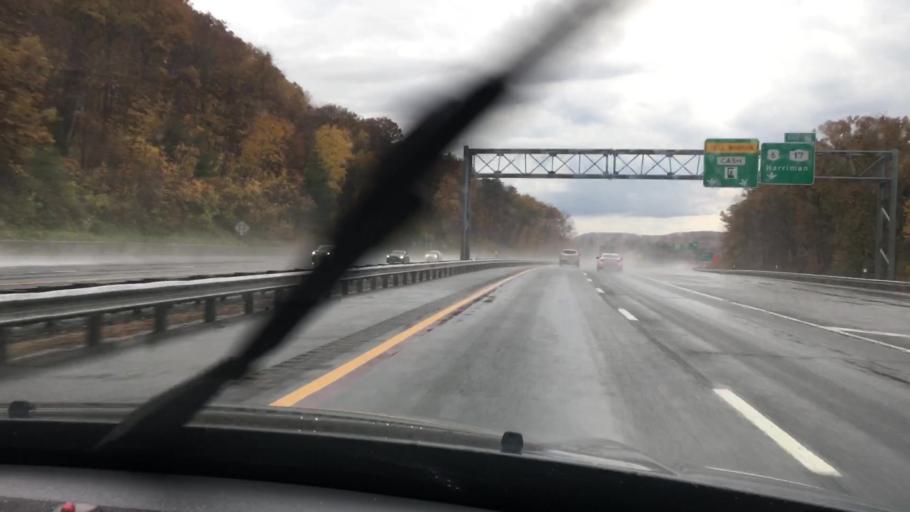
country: US
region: New York
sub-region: Orange County
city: Central Valley
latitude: 41.3154
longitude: -74.1167
